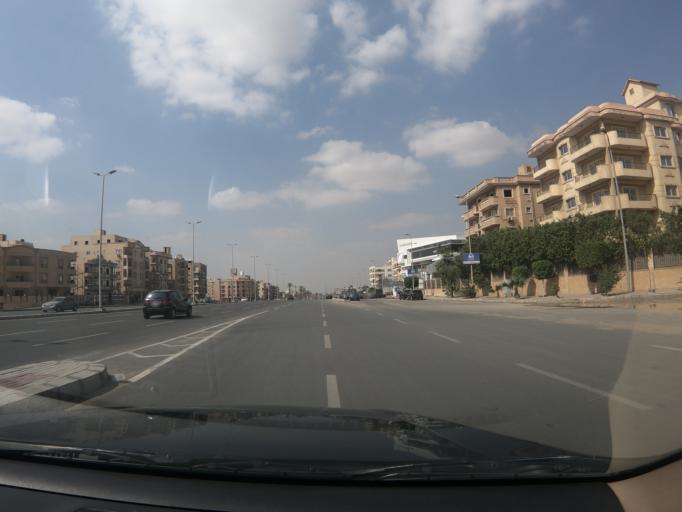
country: EG
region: Muhafazat al Qalyubiyah
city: Al Khankah
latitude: 30.0309
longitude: 31.4753
